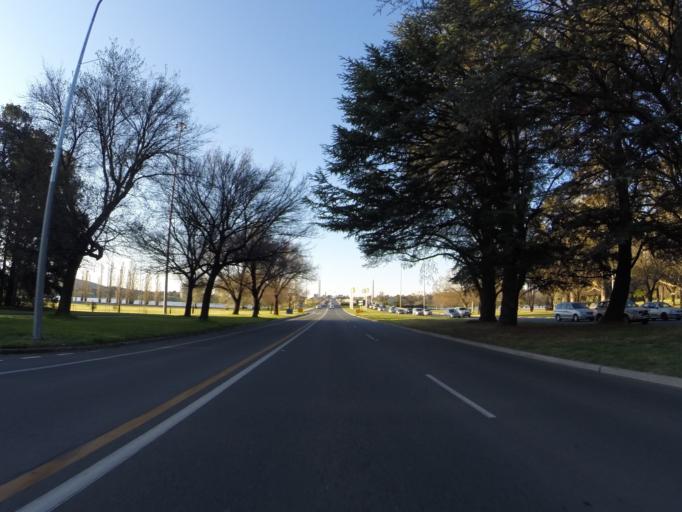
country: AU
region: Australian Capital Territory
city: Canberra
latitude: -35.2975
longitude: 149.1260
